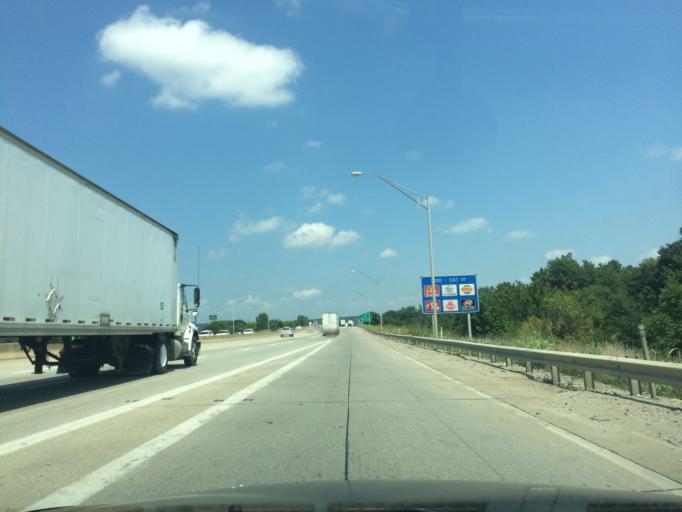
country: US
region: Kentucky
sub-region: Bullitt County
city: Shepherdsville
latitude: 37.9819
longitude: -85.6992
